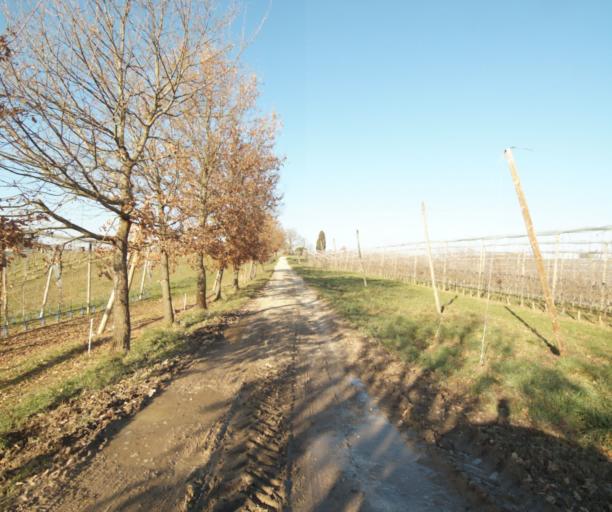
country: FR
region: Midi-Pyrenees
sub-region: Departement du Tarn-et-Garonne
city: Moissac
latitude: 44.1359
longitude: 1.0482
